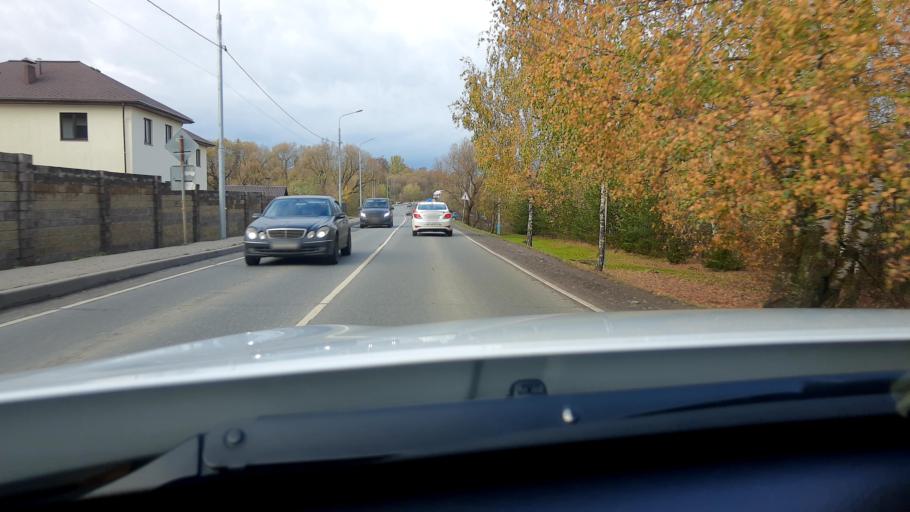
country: RU
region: Moskovskaya
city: Kokoshkino
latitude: 55.5319
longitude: 37.1530
